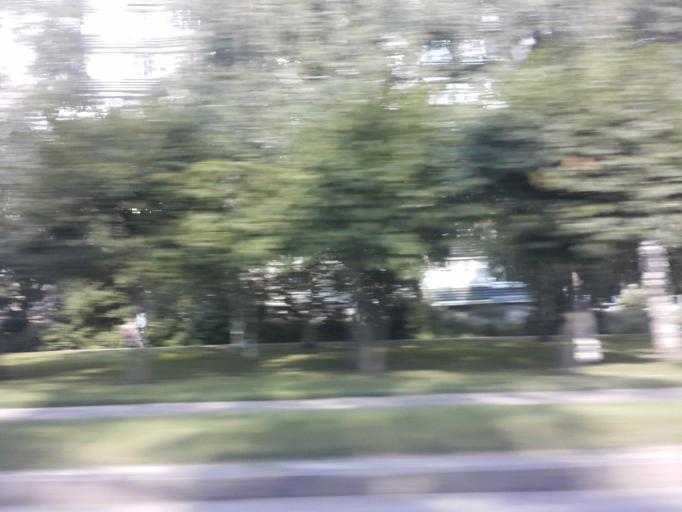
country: RU
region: Tambov
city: Tambov
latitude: 52.7182
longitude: 41.4384
